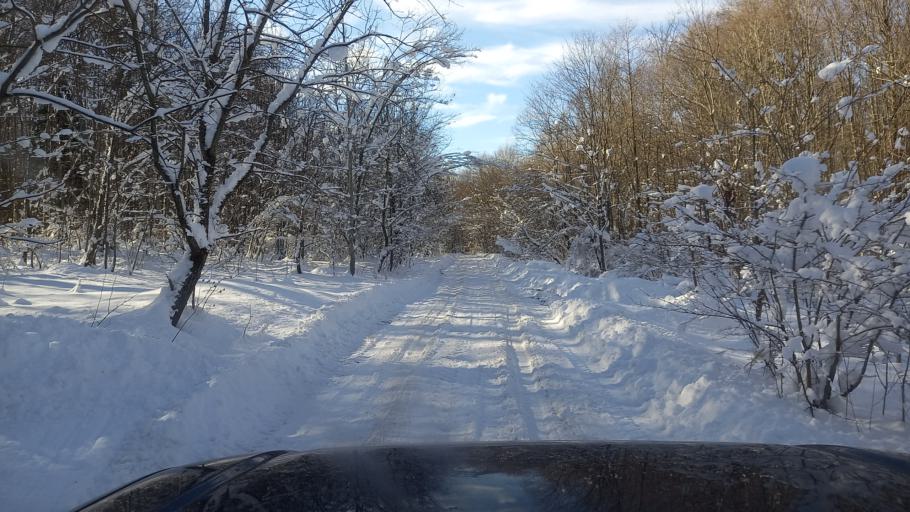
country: RU
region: Adygeya
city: Kamennomostskiy
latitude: 44.1949
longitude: 40.0757
